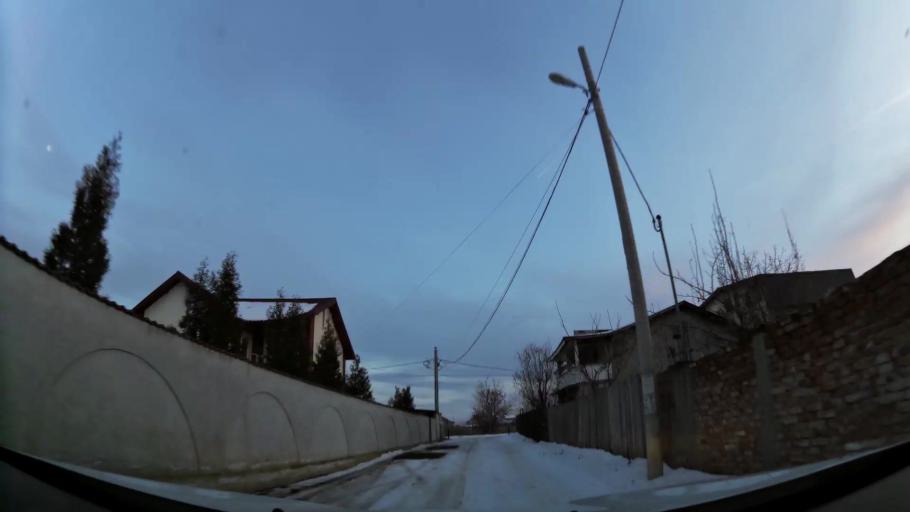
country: RO
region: Ilfov
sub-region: Comuna Magurele
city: Magurele
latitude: 44.3887
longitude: 26.0227
